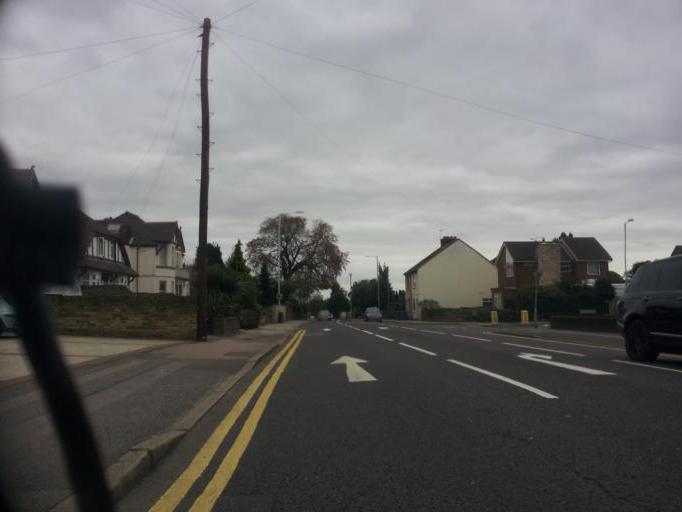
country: GB
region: England
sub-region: Kent
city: Sittingbourne
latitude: 51.3431
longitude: 0.7181
